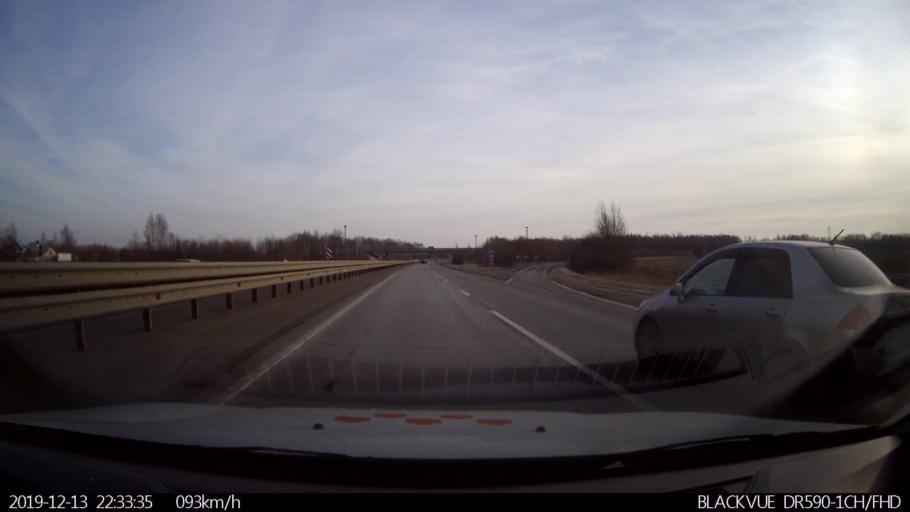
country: RU
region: Nizjnij Novgorod
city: Afonino
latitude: 56.1968
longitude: 44.1171
